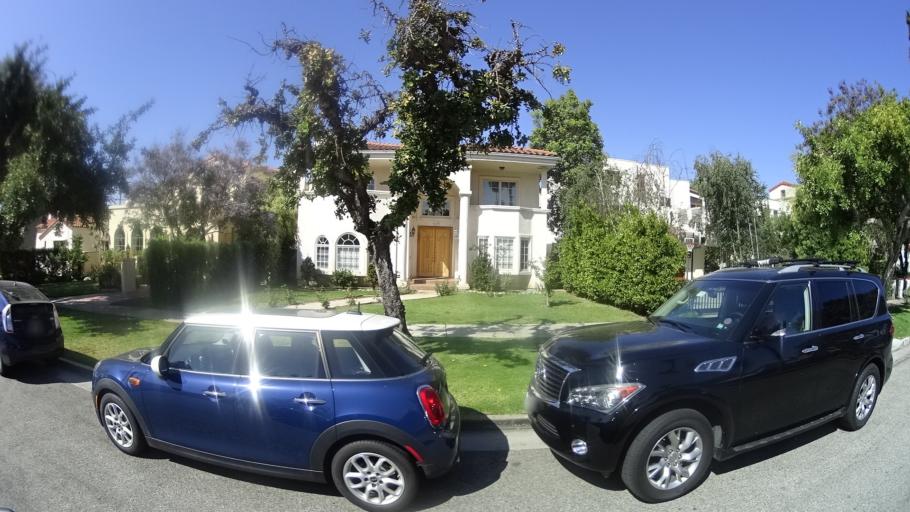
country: US
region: California
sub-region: Los Angeles County
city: Santa Monica
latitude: 34.0313
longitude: -118.5016
